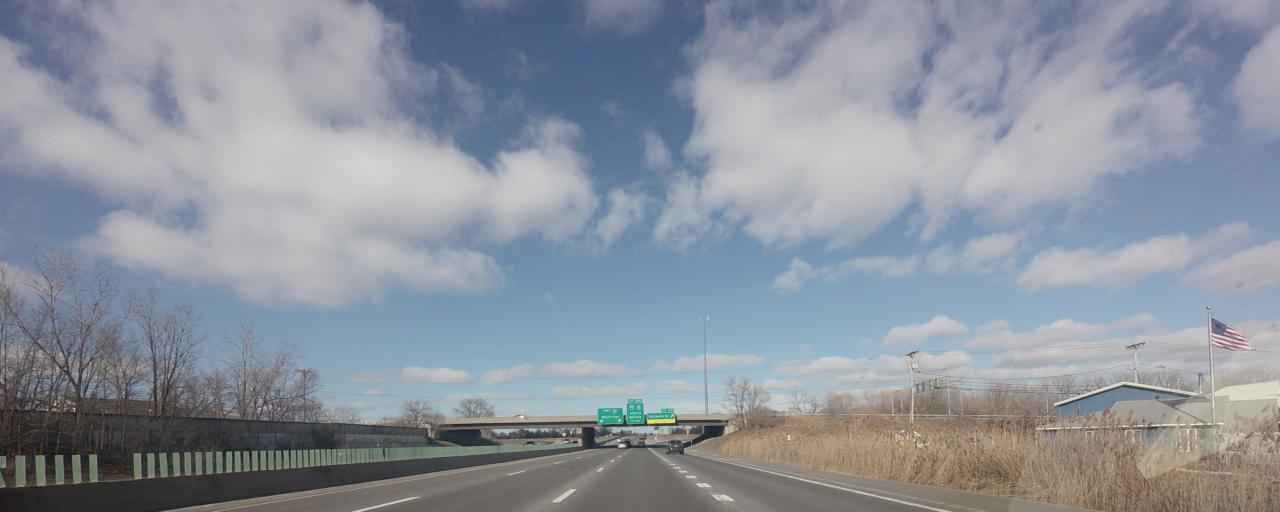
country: US
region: New York
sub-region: Onondaga County
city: Galeville
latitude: 43.0884
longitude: -76.1677
